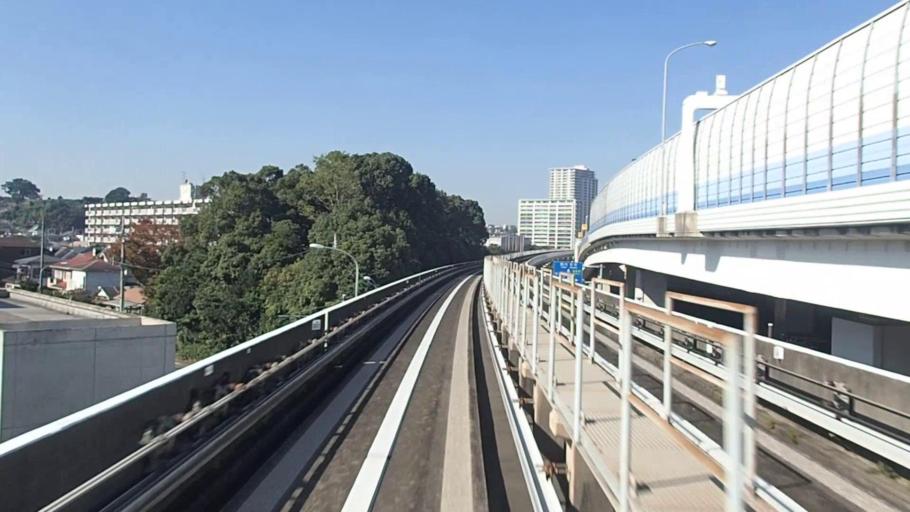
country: JP
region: Kanagawa
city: Yokohama
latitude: 35.3816
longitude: 139.6275
